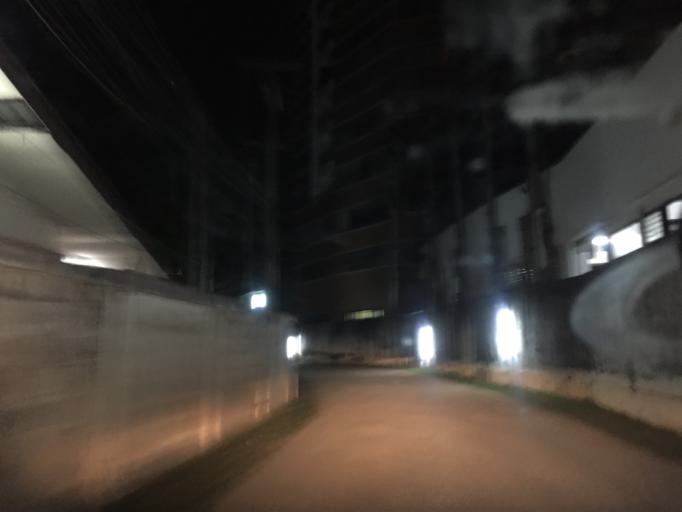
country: TH
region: Chiang Mai
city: Chiang Mai
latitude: 18.8010
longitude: 98.9710
